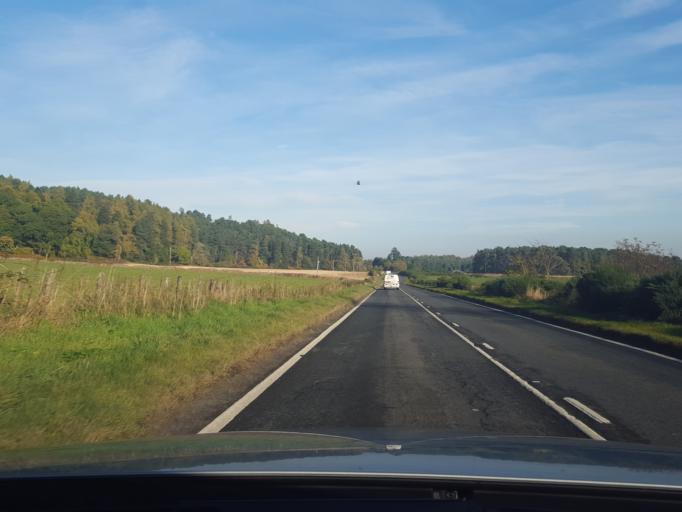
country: GB
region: Scotland
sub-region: Highland
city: Inverness
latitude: 57.4487
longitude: -4.2863
